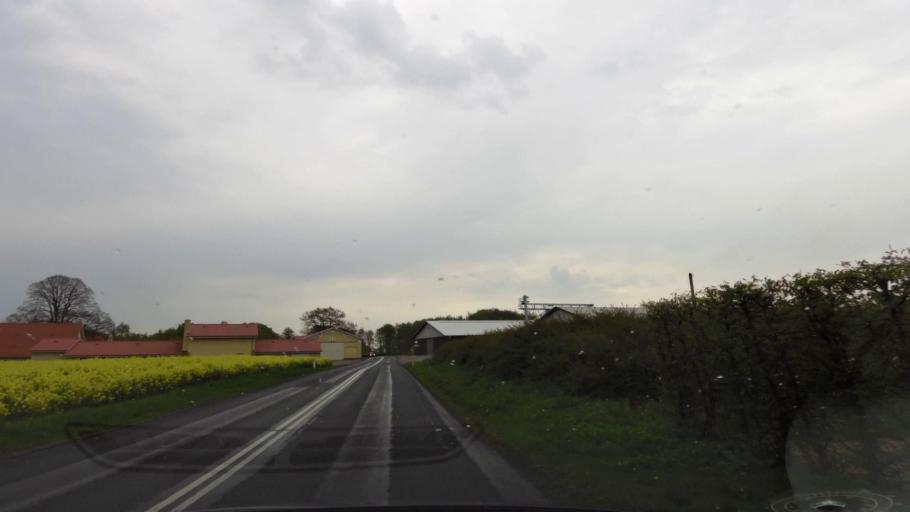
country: DK
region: South Denmark
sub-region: Svendborg Kommune
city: Svendborg
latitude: 55.1686
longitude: 10.6293
